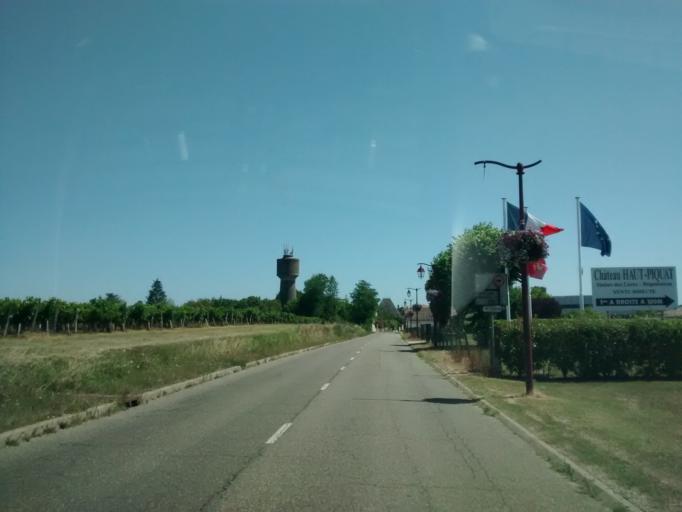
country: FR
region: Aquitaine
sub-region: Departement de la Gironde
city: Lussac
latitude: 44.9497
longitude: -0.1022
